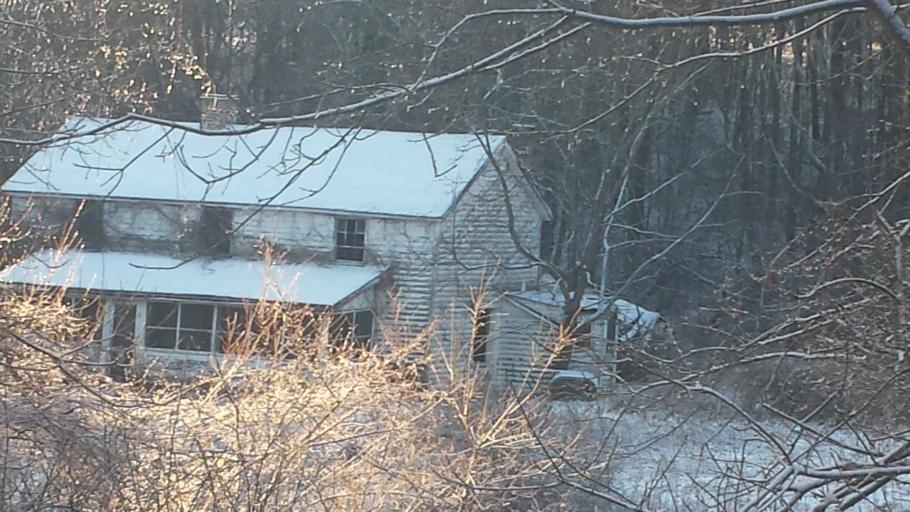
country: US
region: Virginia
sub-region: Floyd County
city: Floyd
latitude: 36.9771
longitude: -80.2231
